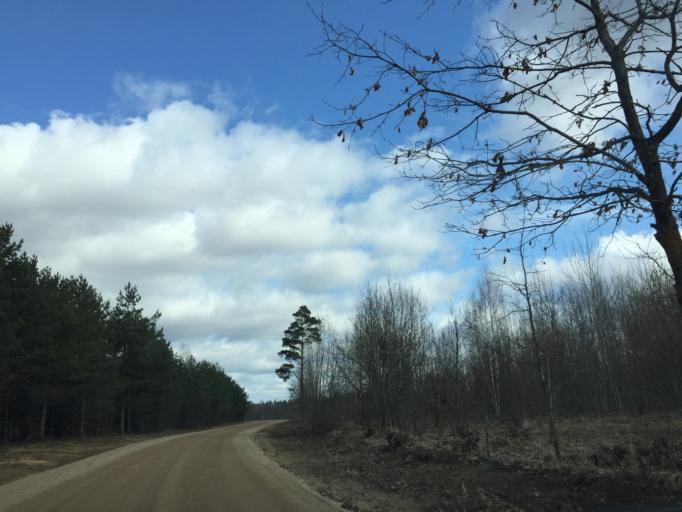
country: LV
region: Vecumnieki
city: Vecumnieki
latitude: 56.5925
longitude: 24.6095
